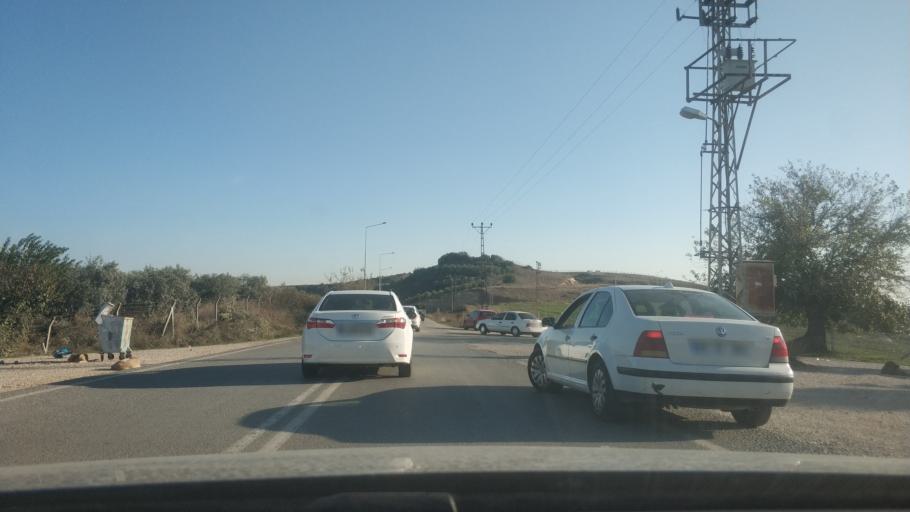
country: TR
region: Adana
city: Adana
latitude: 37.0980
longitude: 35.3048
